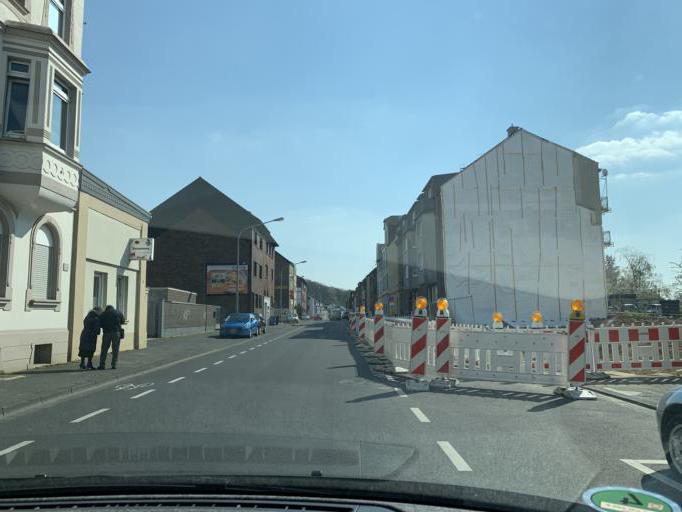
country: DE
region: North Rhine-Westphalia
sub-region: Regierungsbezirk Dusseldorf
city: Monchengladbach
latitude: 51.1464
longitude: 6.4565
